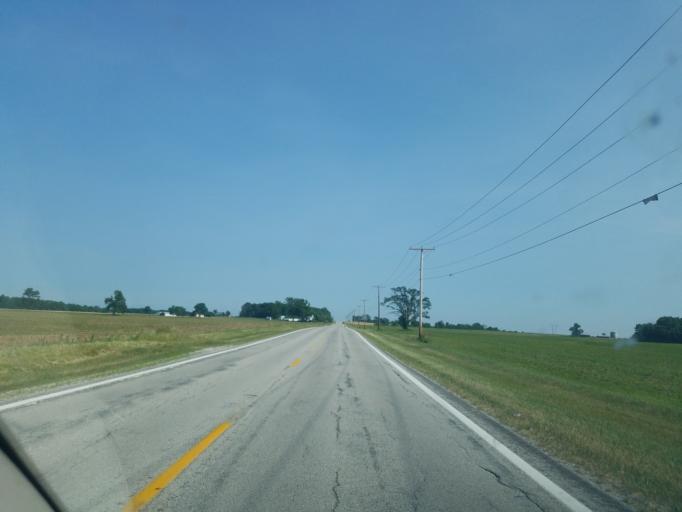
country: US
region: Ohio
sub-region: Wyandot County
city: Carey
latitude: 41.0197
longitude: -83.2900
